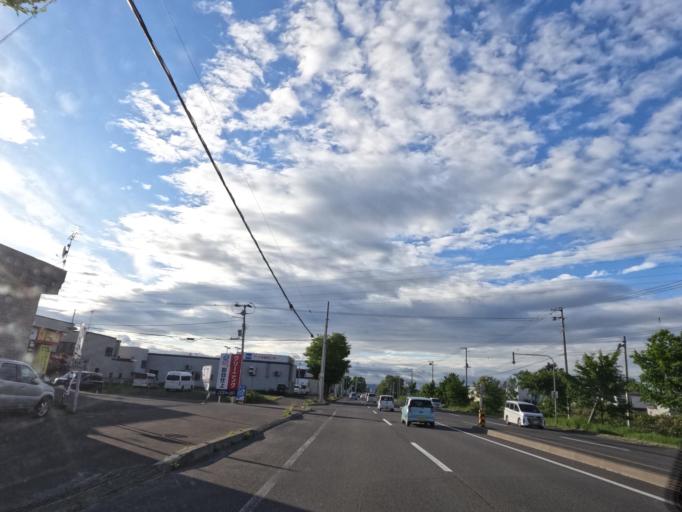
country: JP
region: Hokkaido
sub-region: Asahikawa-shi
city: Asahikawa
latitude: 43.7406
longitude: 142.3597
